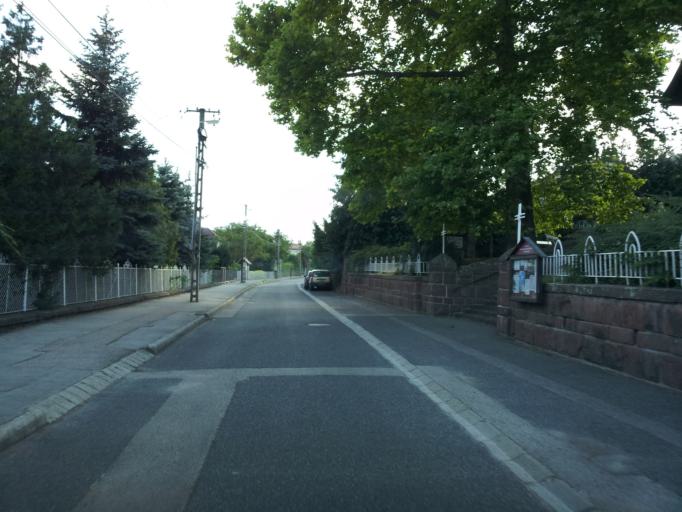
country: HU
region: Veszprem
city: Balatonalmadi
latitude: 47.0268
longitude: 18.0097
